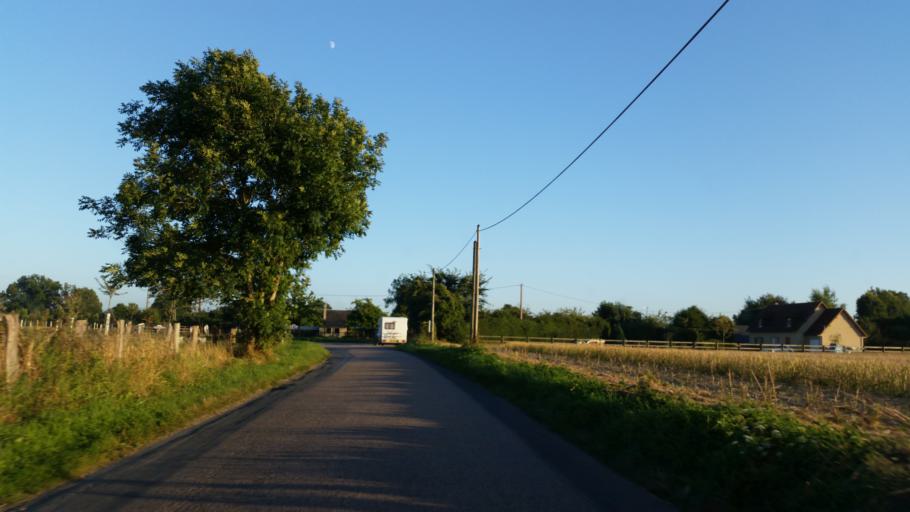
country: FR
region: Lower Normandy
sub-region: Departement du Calvados
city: Equemauville
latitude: 49.3842
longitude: 0.2266
